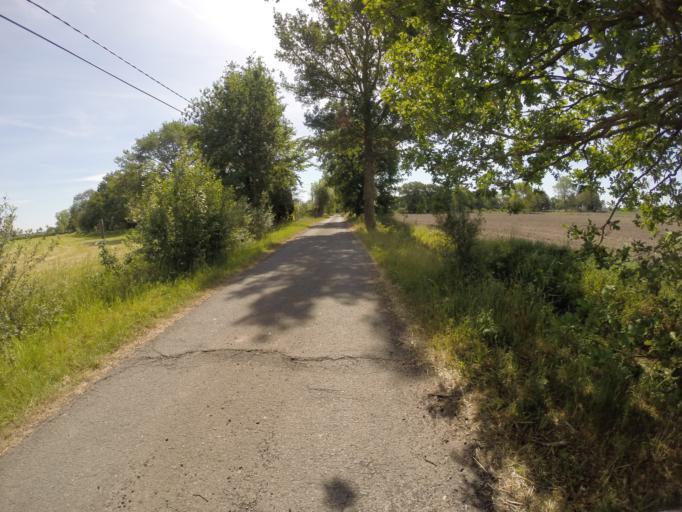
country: BE
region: Flanders
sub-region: Provincie West-Vlaanderen
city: Beernem
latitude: 51.1456
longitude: 3.3690
